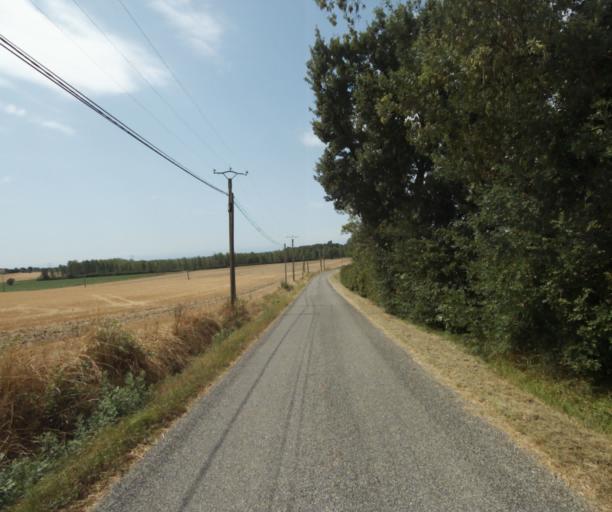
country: FR
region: Midi-Pyrenees
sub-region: Departement de la Haute-Garonne
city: Saint-Felix-Lauragais
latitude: 43.4285
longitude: 1.9192
